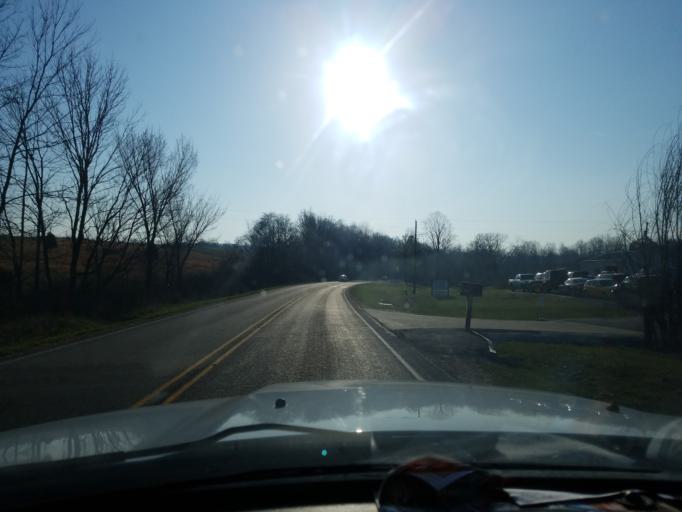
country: US
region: Indiana
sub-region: Owen County
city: Spencer
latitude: 39.3420
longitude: -86.9013
